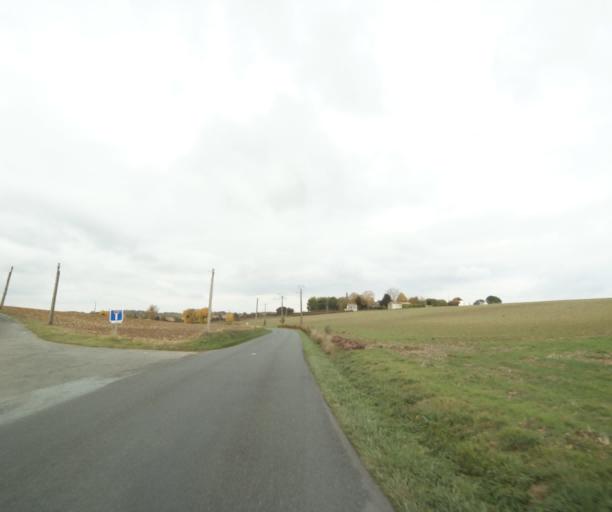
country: FR
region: Poitou-Charentes
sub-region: Departement de la Charente-Maritime
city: Bussac-sur-Charente
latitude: 45.7750
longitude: -0.6727
